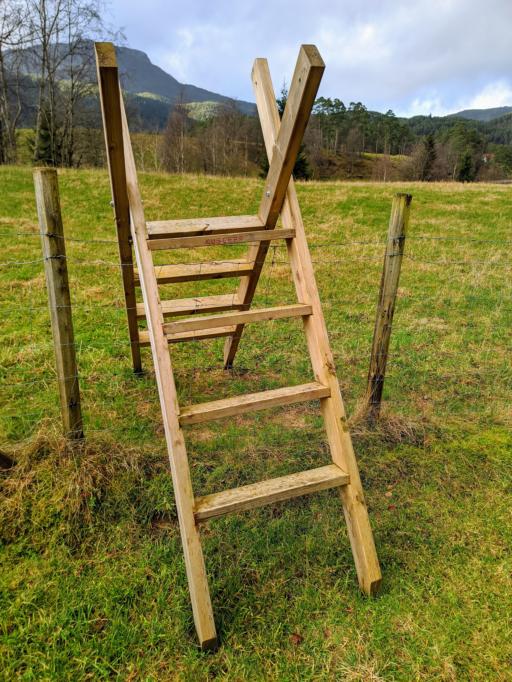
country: NO
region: Rogaland
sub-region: Suldal
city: Sand
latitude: 59.4651
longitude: 6.4260
